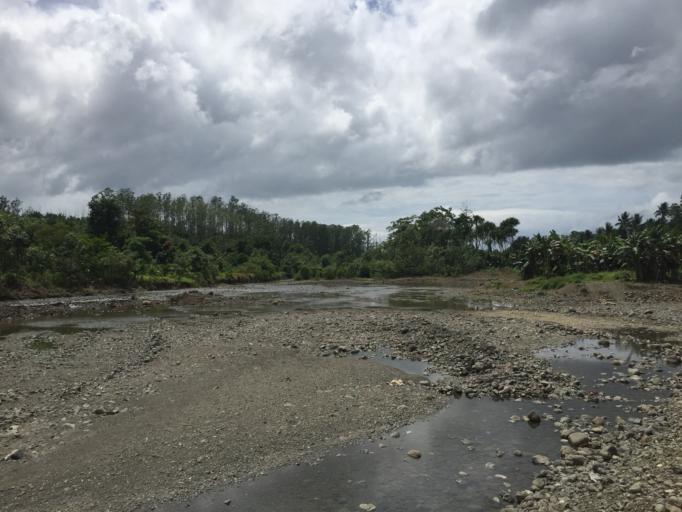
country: PG
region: Milne Bay
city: Alotau
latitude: -10.2956
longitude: 150.3148
